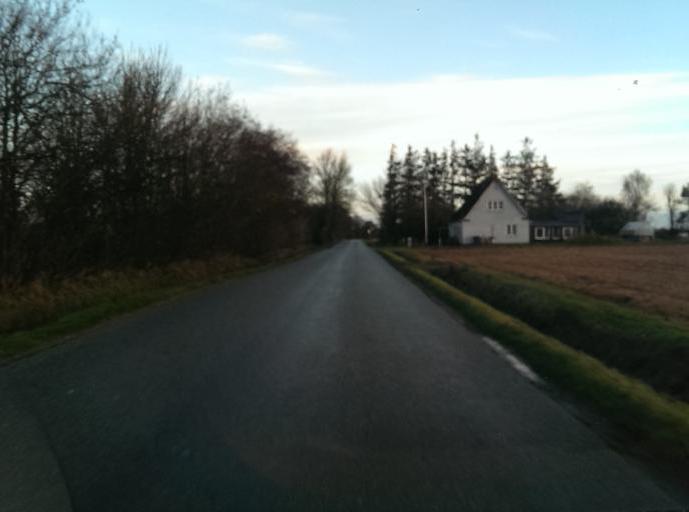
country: DK
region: South Denmark
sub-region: Esbjerg Kommune
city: Tjaereborg
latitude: 55.4764
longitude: 8.6310
